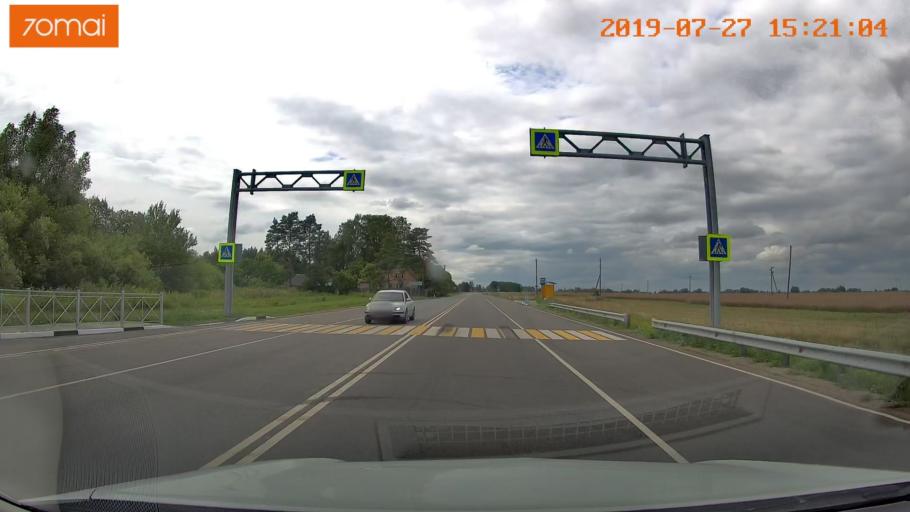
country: LT
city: Kybartai
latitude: 54.6329
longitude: 22.6912
